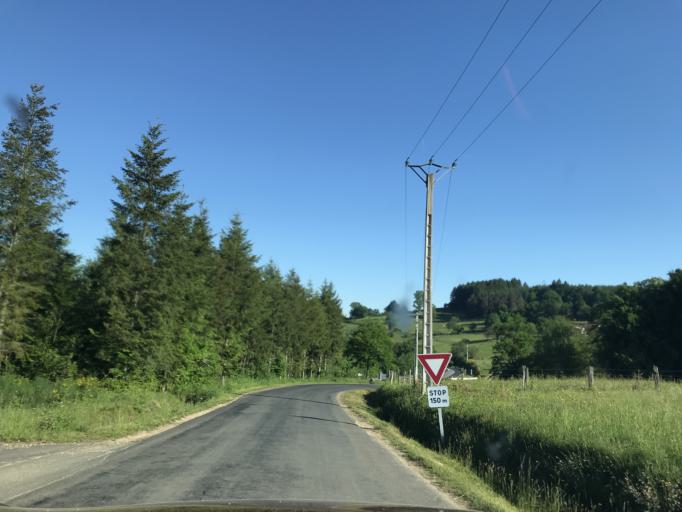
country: FR
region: Auvergne
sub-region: Departement du Puy-de-Dome
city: Job
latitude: 45.6589
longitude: 3.6611
